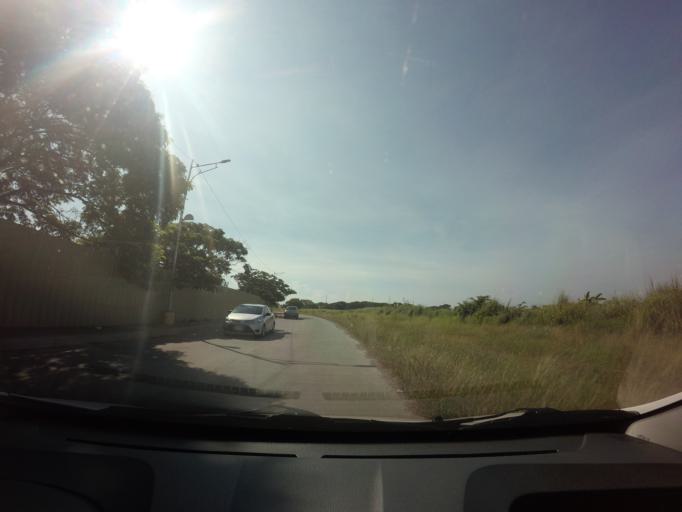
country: PH
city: Sambayanihan People's Village
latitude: 14.4773
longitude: 120.9871
